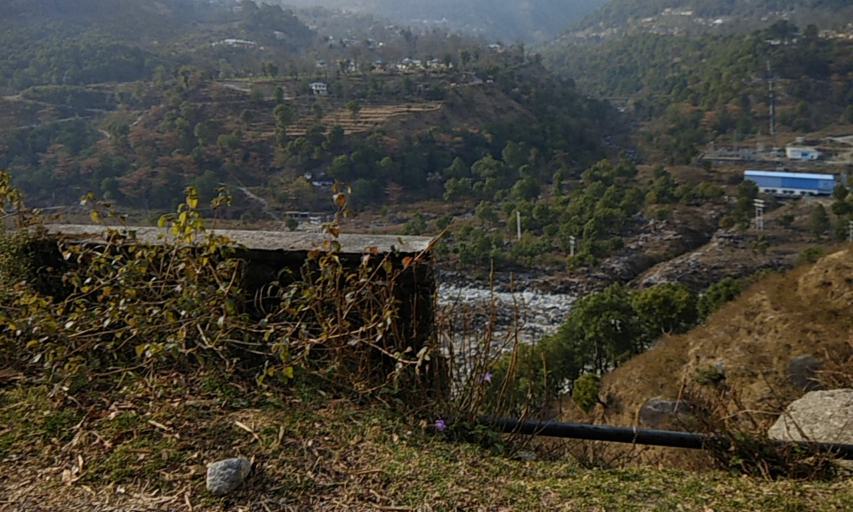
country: IN
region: Himachal Pradesh
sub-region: Kangra
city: Palampur
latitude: 32.1407
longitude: 76.5380
